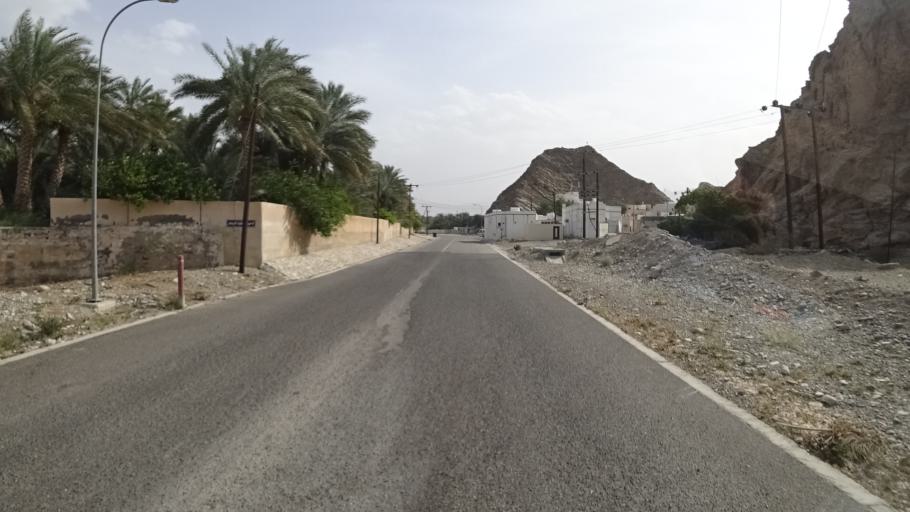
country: OM
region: Muhafazat Masqat
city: Bawshar
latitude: 23.3932
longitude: 58.5197
